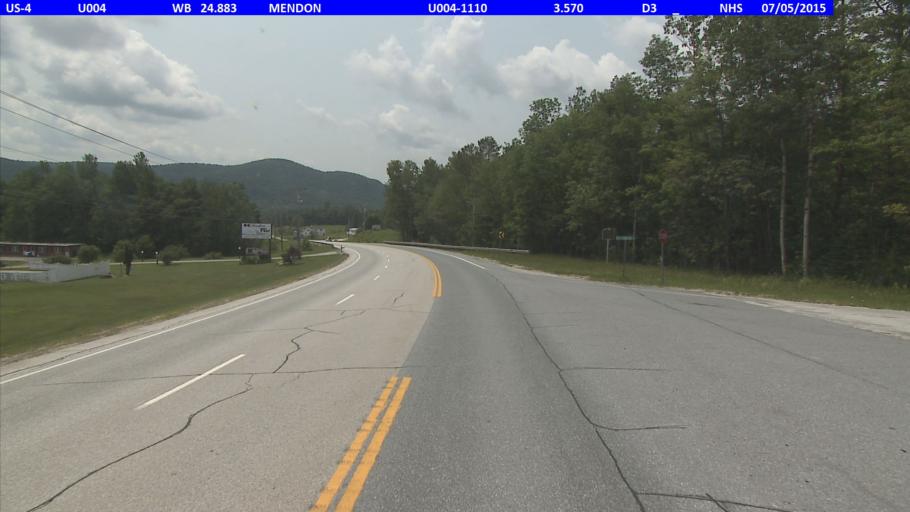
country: US
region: Vermont
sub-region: Rutland County
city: Rutland
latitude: 43.6554
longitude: -72.8864
